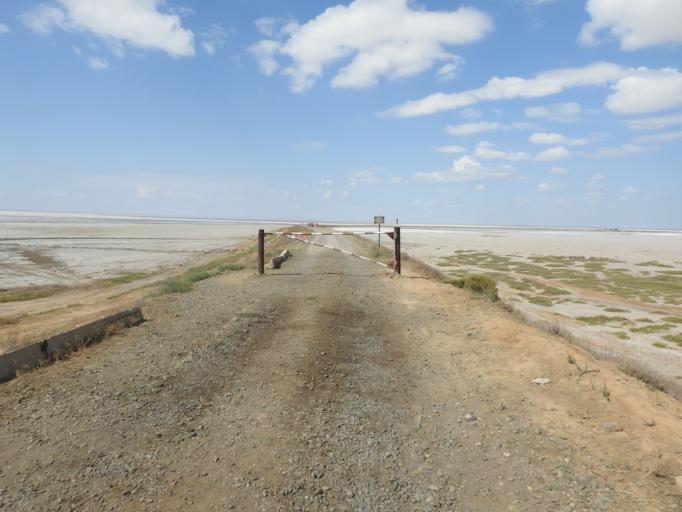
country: RU
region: Volgograd
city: El'ton
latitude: 49.1552
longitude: 46.8047
